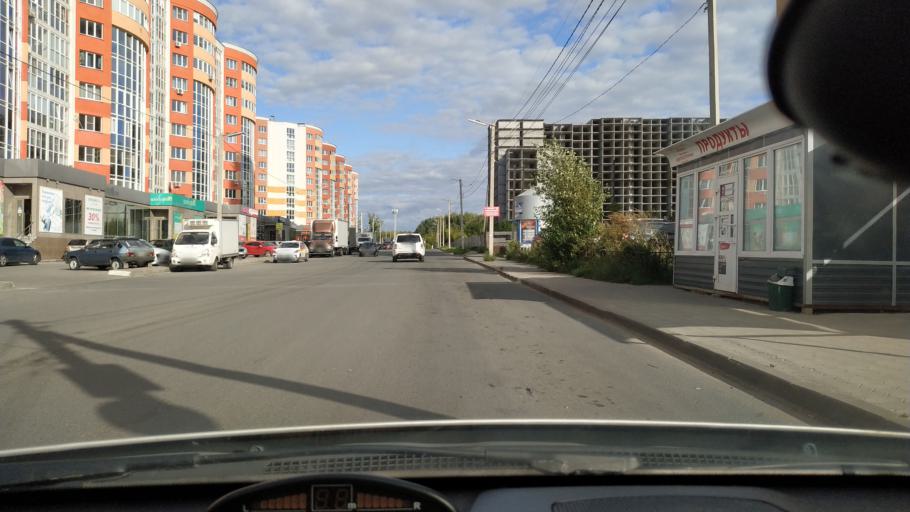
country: RU
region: Rjazan
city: Ryazan'
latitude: 54.6046
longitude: 39.7380
